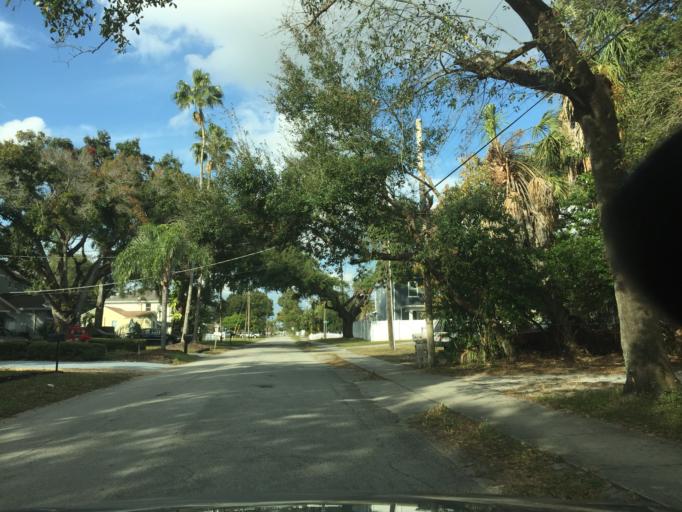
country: US
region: Florida
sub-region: Hillsborough County
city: Tampa
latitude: 27.9461
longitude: -82.4892
